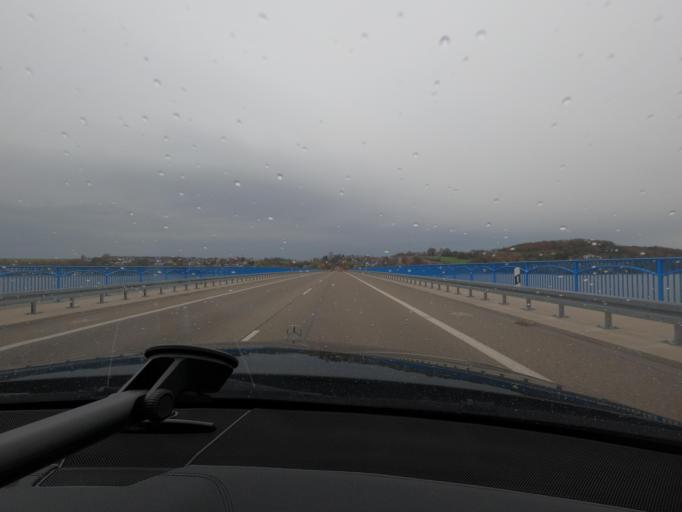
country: DE
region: North Rhine-Westphalia
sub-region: Regierungsbezirk Arnsberg
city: Mohnesee
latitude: 51.4841
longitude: 8.0871
